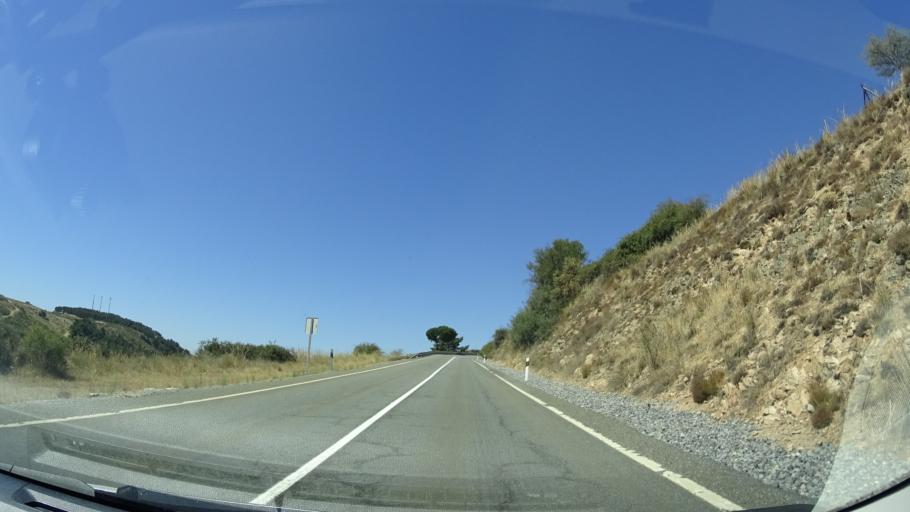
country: ES
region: Castille and Leon
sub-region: Provincia de Avila
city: Navalperal de Pinares
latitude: 40.6136
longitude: -4.4971
